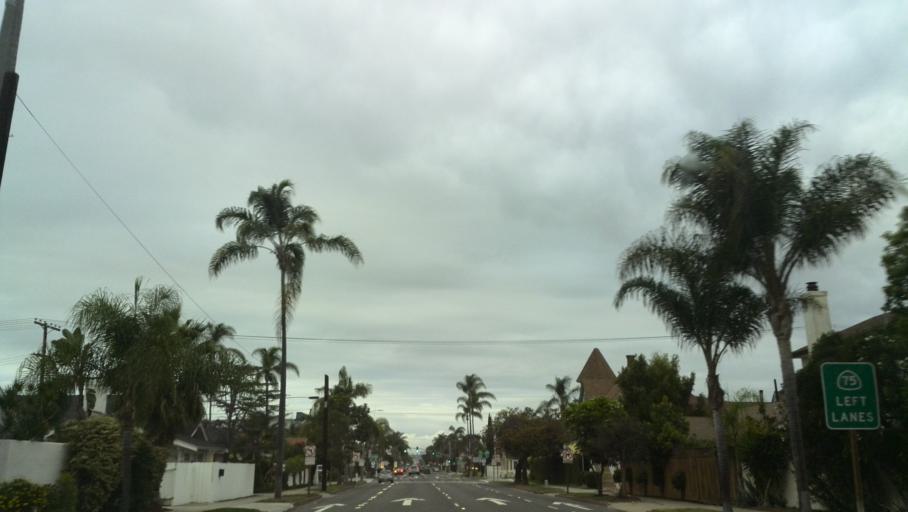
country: US
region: California
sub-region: San Diego County
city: Coronado
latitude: 32.6950
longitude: -117.1717
